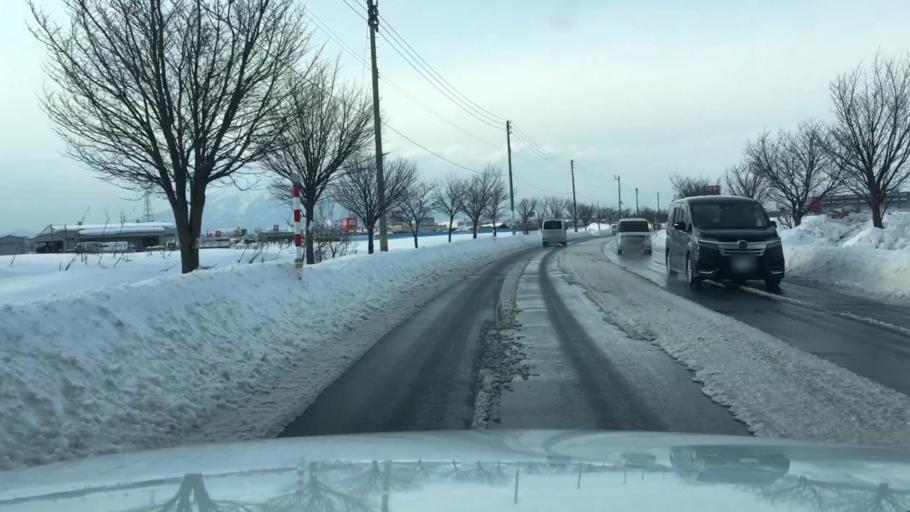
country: JP
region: Aomori
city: Hirosaki
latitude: 40.5946
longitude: 140.5188
